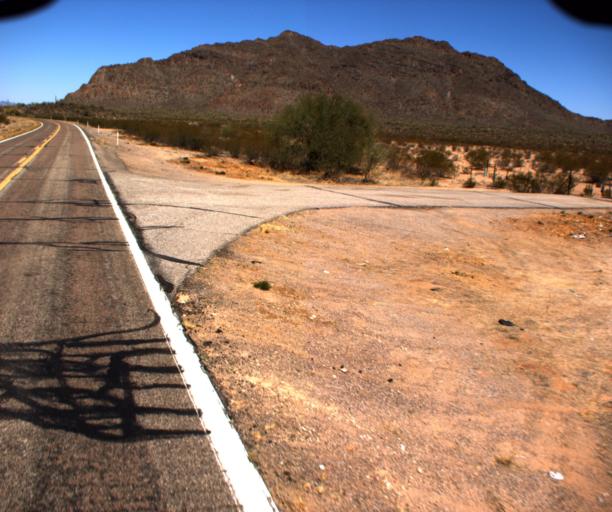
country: US
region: Arizona
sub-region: Pima County
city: Ajo
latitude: 32.2231
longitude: -112.6757
